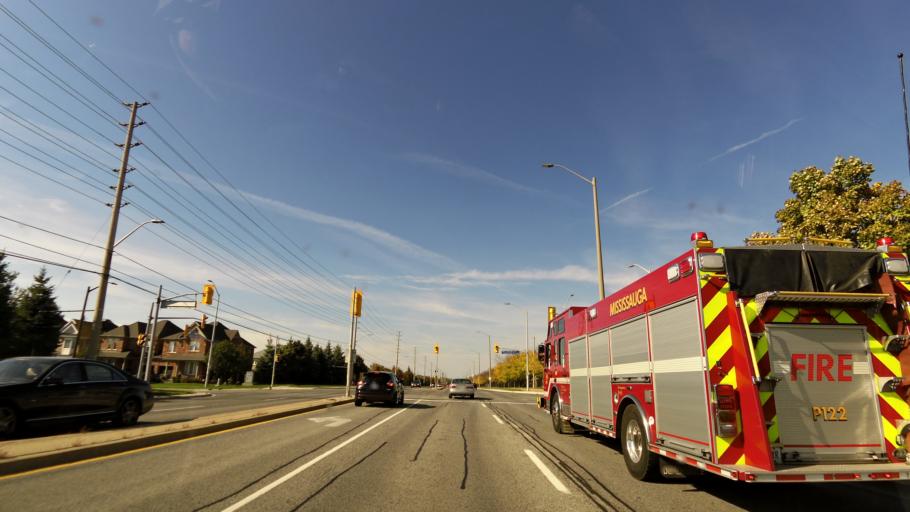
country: CA
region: Ontario
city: Mississauga
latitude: 43.5628
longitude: -79.7362
